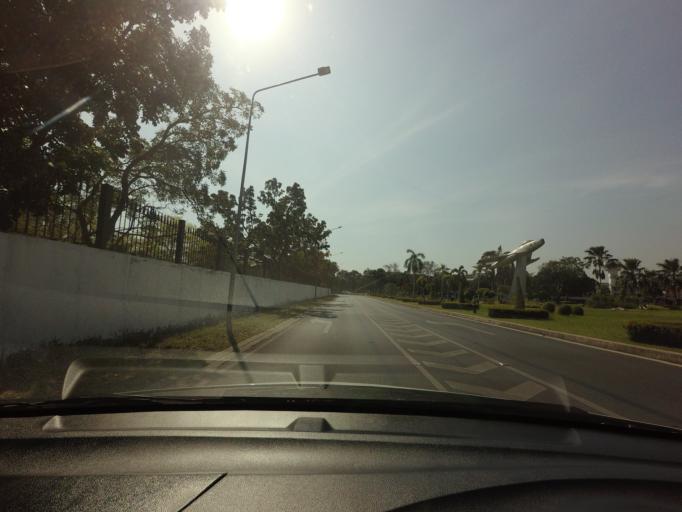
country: TH
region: Bangkok
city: Sai Mai
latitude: 13.9260
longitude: 100.6220
